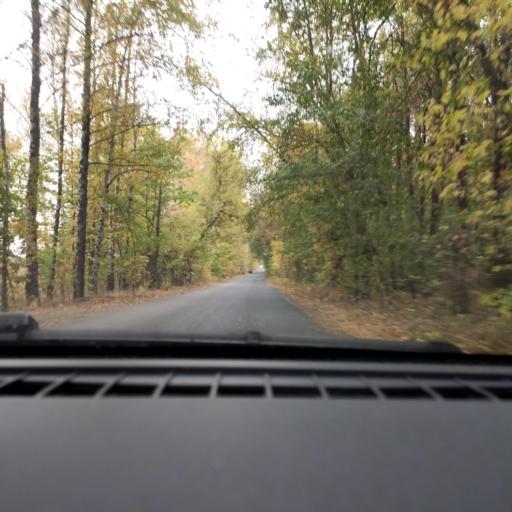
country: RU
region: Voronezj
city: Somovo
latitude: 51.6863
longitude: 39.3001
